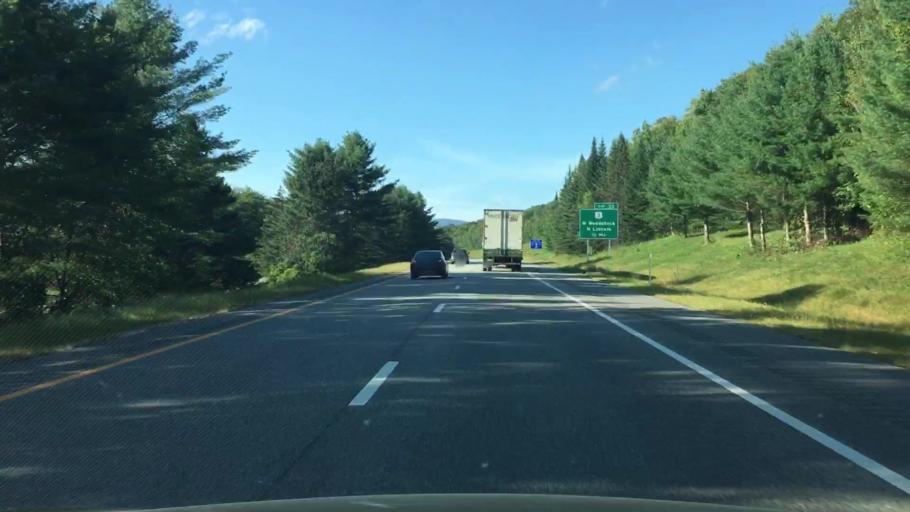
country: US
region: New Hampshire
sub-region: Grafton County
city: Woodstock
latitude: 44.0504
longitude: -71.6813
